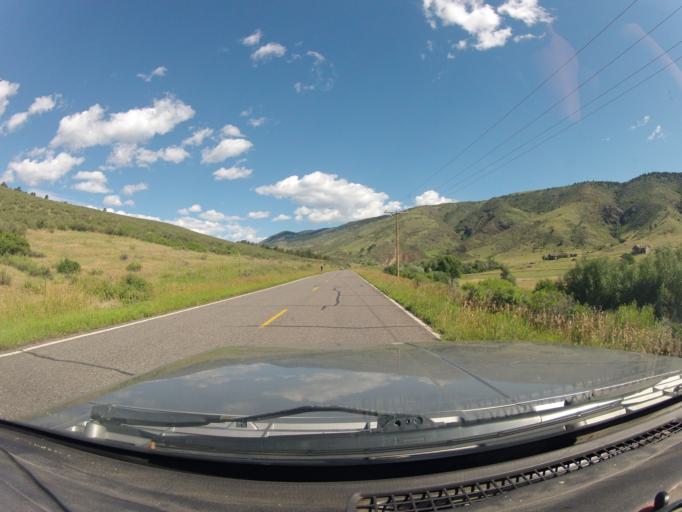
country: US
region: Colorado
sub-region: Larimer County
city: Laporte
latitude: 40.5036
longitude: -105.2276
